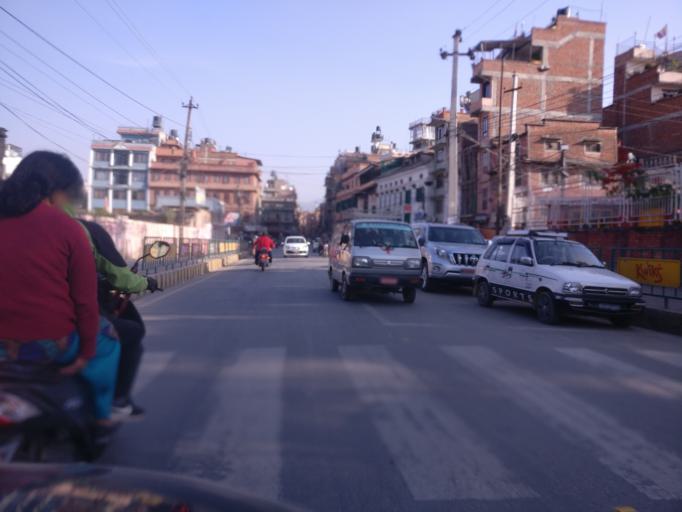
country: NP
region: Central Region
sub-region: Bagmati Zone
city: Patan
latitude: 27.6762
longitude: 85.3179
